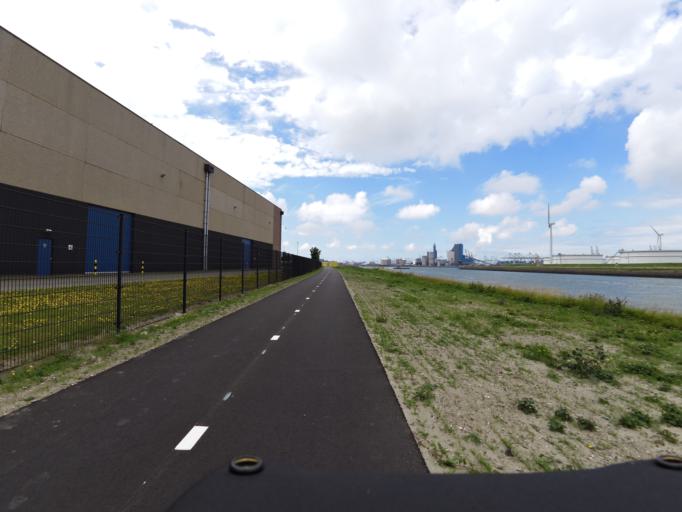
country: NL
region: South Holland
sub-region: Gemeente Rotterdam
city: Hoek van Holland
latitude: 51.9379
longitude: 4.0949
